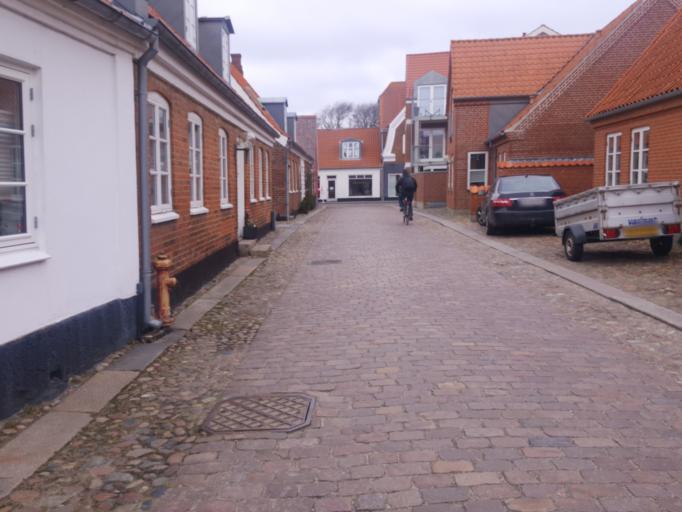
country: DK
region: Central Jutland
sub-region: Ringkobing-Skjern Kommune
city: Ringkobing
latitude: 56.0905
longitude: 8.2463
